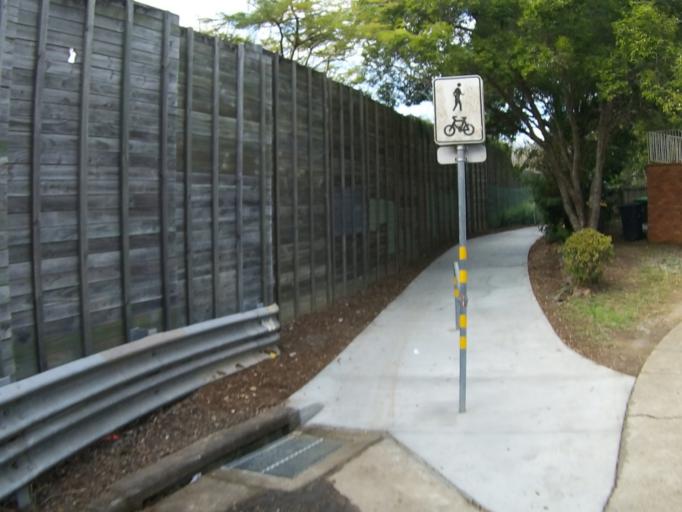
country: AU
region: Queensland
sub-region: Brisbane
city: Greenslopes
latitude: -27.5214
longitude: 153.0523
